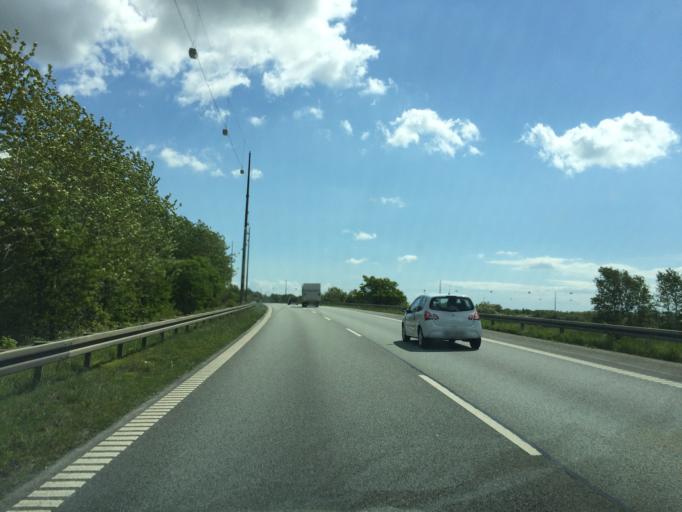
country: DK
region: Capital Region
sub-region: Vallensbaek Kommune
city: Vallensbaek
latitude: 55.6409
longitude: 12.3412
